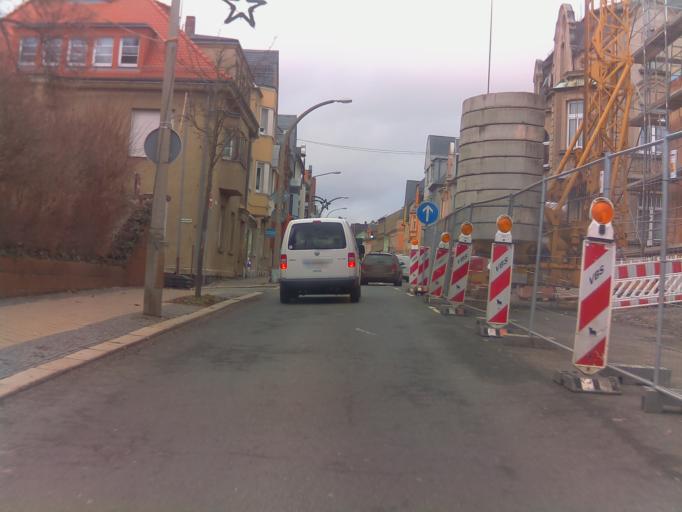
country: DE
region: Thuringia
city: Zeulenroda
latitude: 50.6496
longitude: 11.9812
